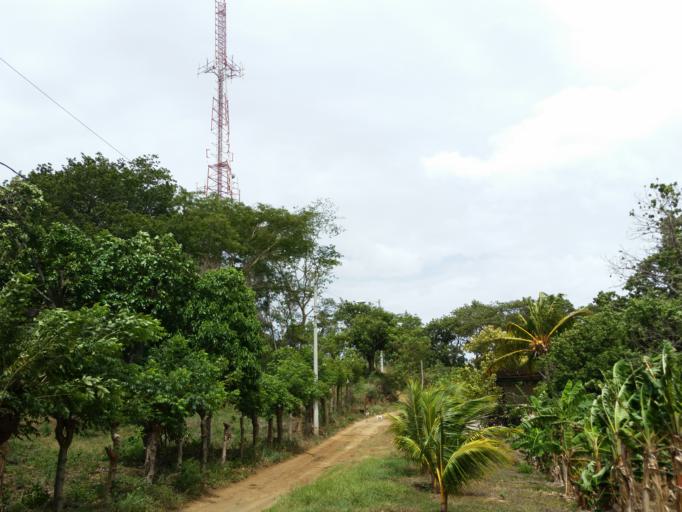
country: NI
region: Managua
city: Managua
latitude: 12.0796
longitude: -86.2511
